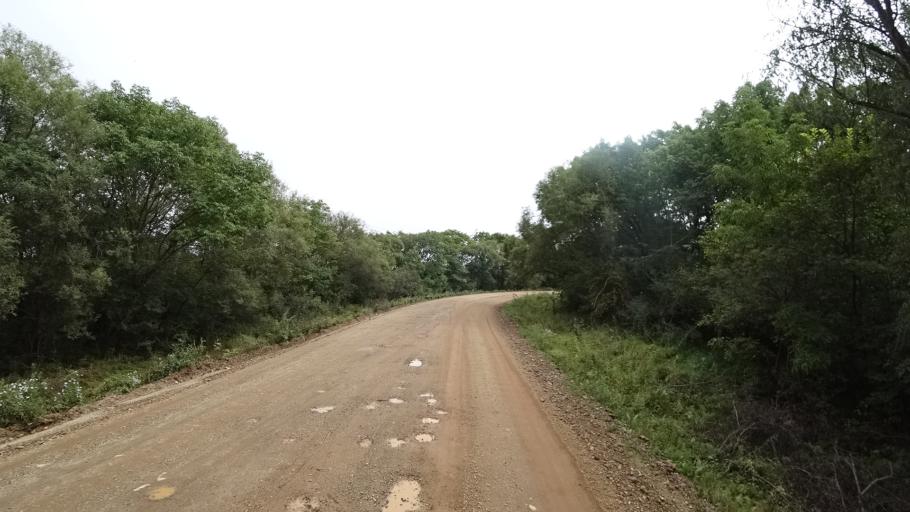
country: RU
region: Primorskiy
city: Lyalichi
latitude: 44.0811
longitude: 132.4503
